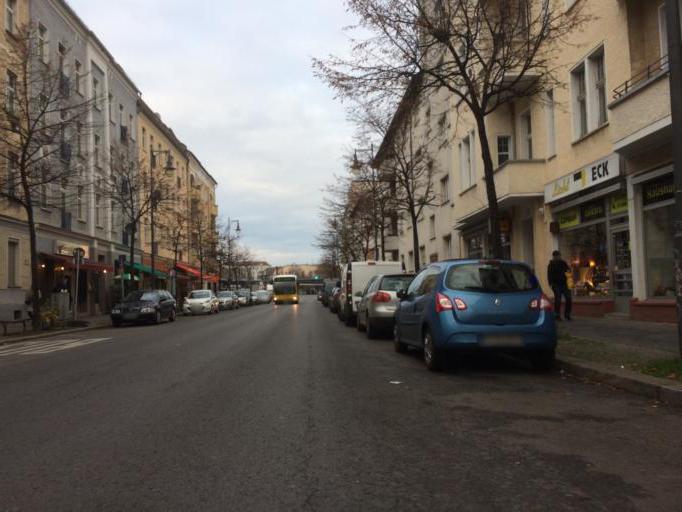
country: DE
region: Berlin
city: Lichtenberg
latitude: 52.5082
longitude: 13.4972
